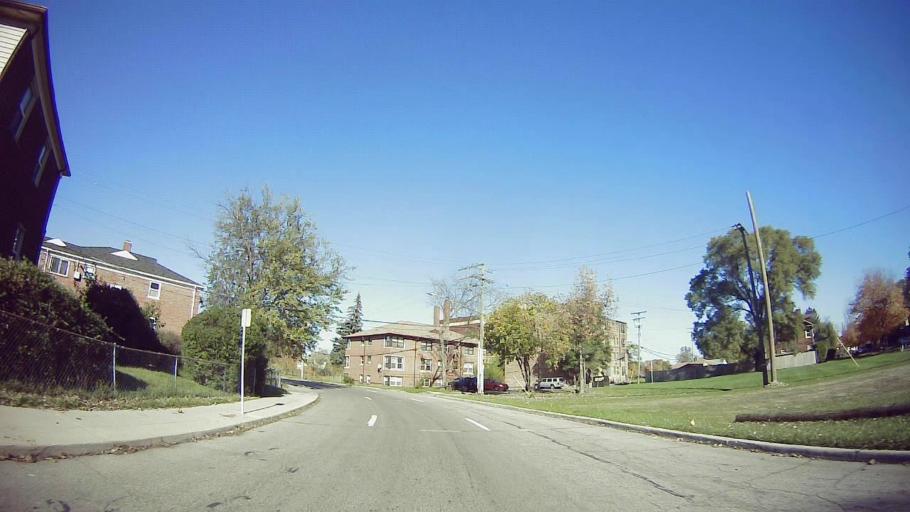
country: US
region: Michigan
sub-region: Wayne County
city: Highland Park
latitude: 42.3837
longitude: -83.1077
